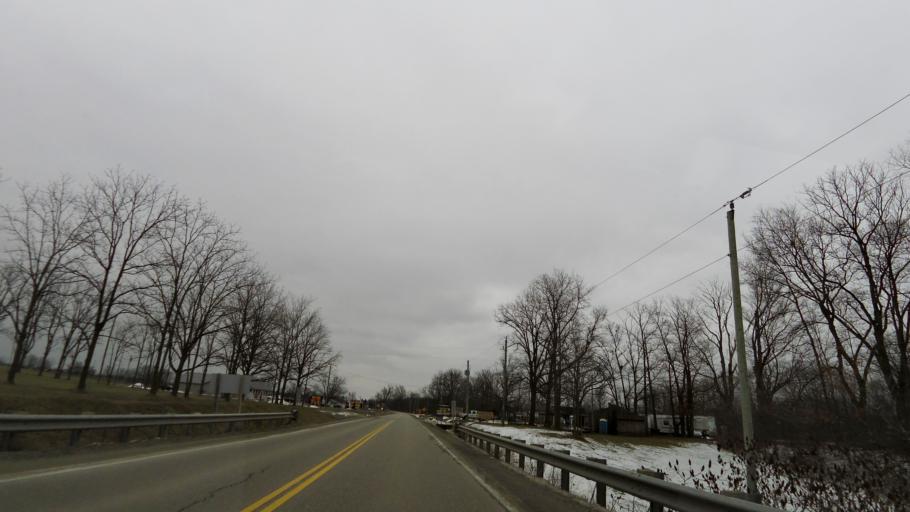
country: CA
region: Ontario
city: Ancaster
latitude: 43.1014
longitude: -80.0895
